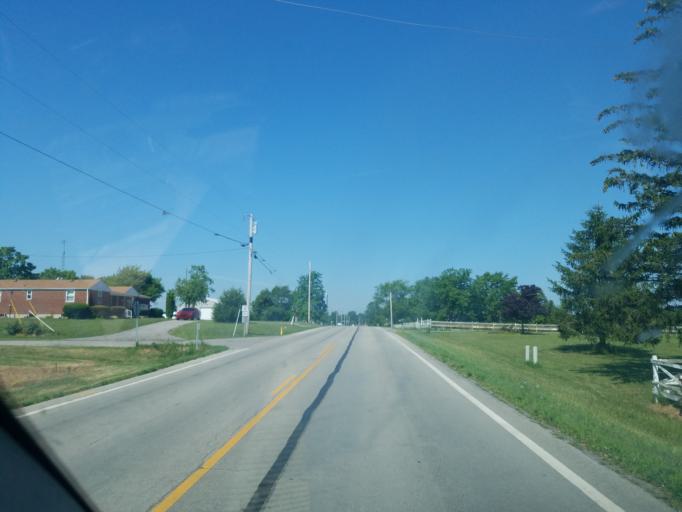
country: US
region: Ohio
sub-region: Logan County
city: Russells Point
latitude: 40.4643
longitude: -83.8214
